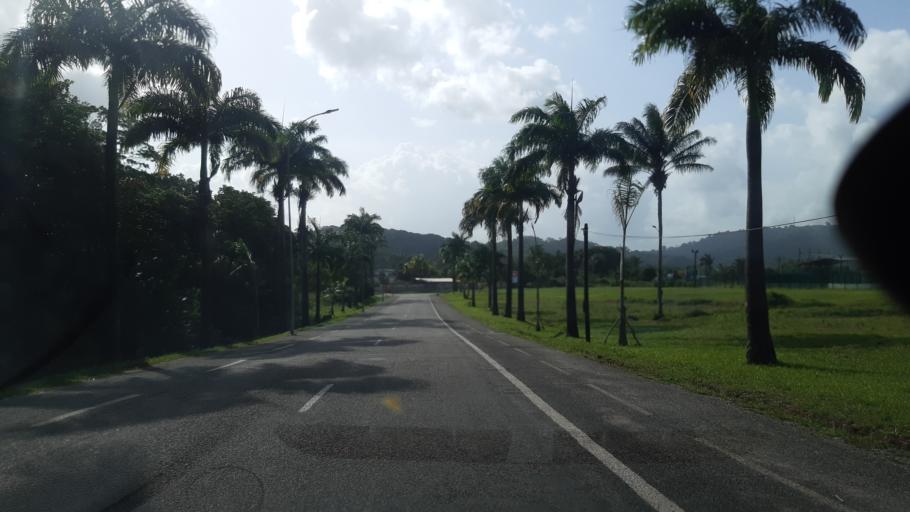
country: GF
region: Guyane
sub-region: Guyane
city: Matoury
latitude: 4.8457
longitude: -52.3286
